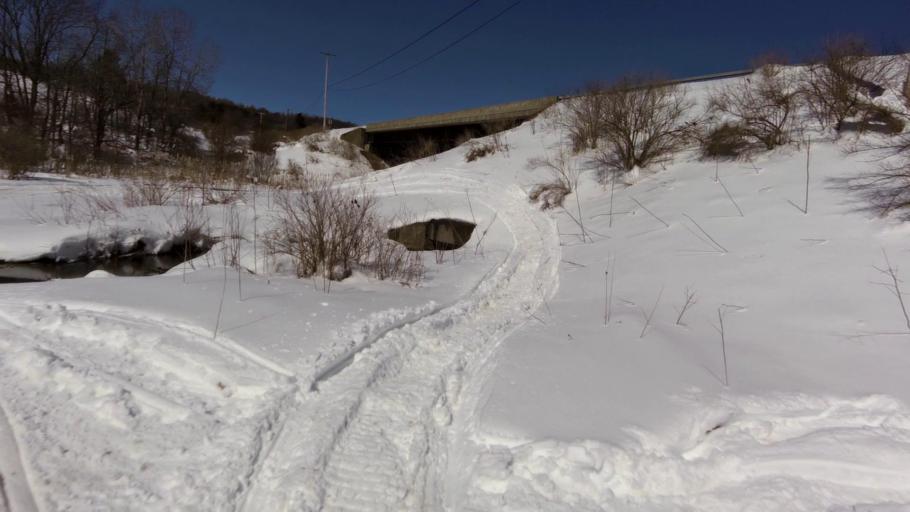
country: US
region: New York
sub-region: Wyoming County
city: Arcade
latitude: 42.4426
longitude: -78.3383
